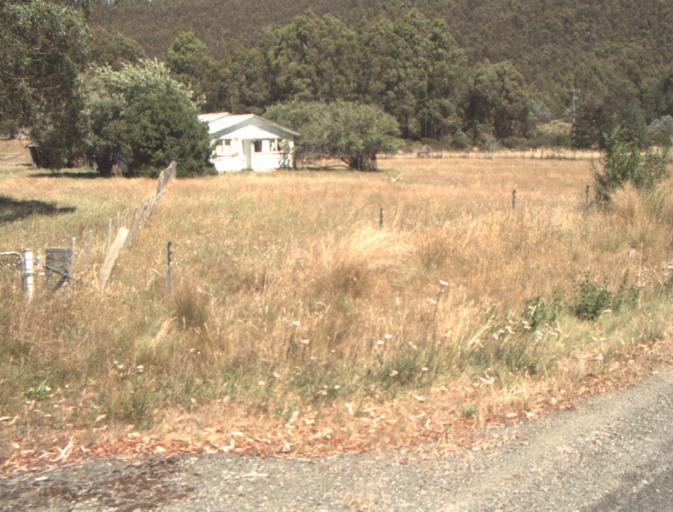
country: AU
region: Tasmania
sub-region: Dorset
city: Scottsdale
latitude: -41.3105
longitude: 147.3761
